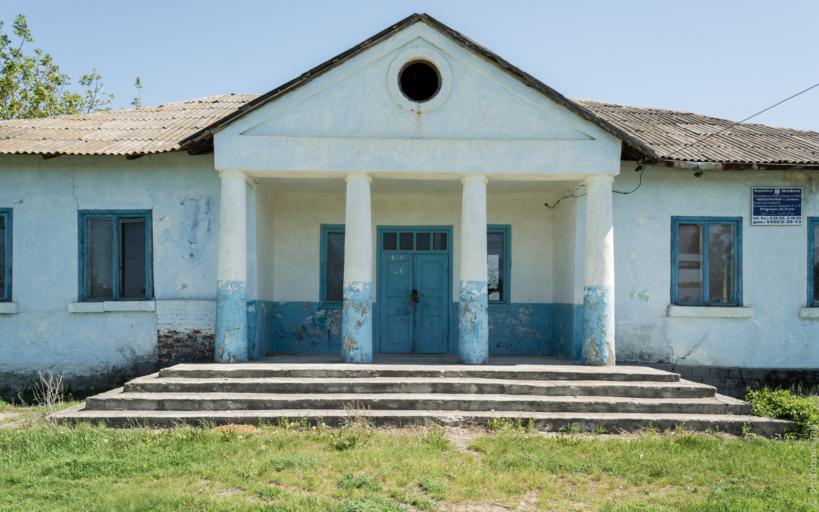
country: MD
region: Balti
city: Balti
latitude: 47.8295
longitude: 27.8376
